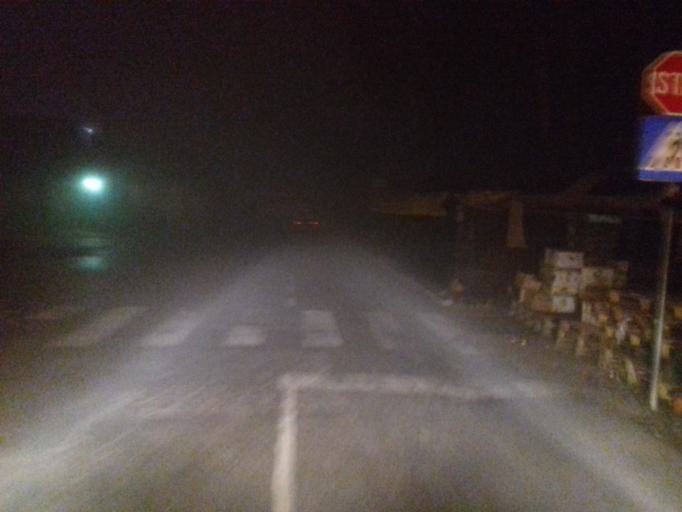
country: BA
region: Federation of Bosnia and Herzegovina
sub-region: Kanton Sarajevo
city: Sarajevo
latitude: 43.8452
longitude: 18.3342
